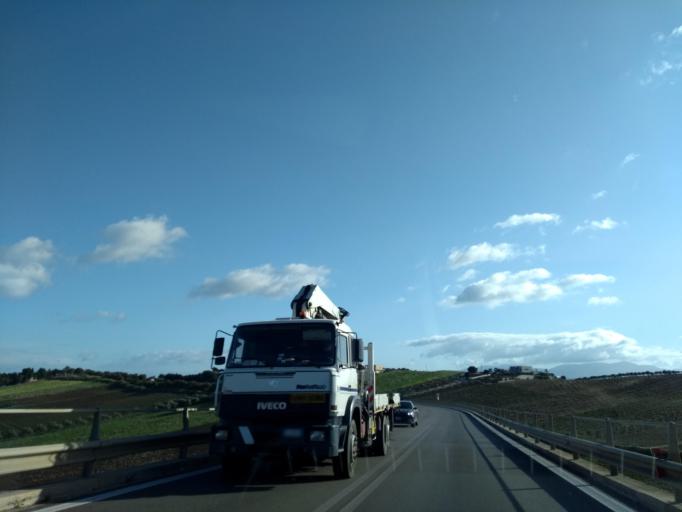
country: IT
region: Sicily
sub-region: Trapani
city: Alcamo
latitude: 38.0061
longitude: 12.9601
